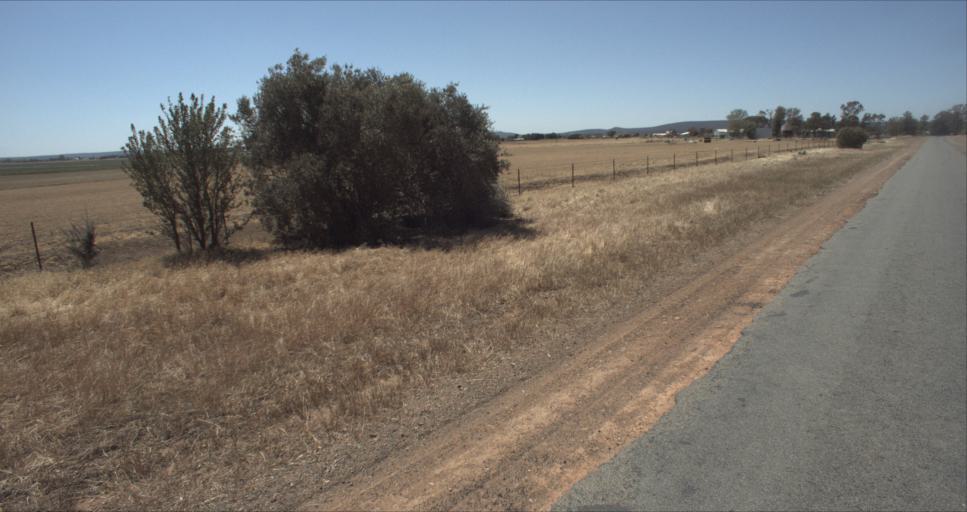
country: AU
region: New South Wales
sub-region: Leeton
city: Leeton
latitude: -34.5409
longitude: 146.4376
